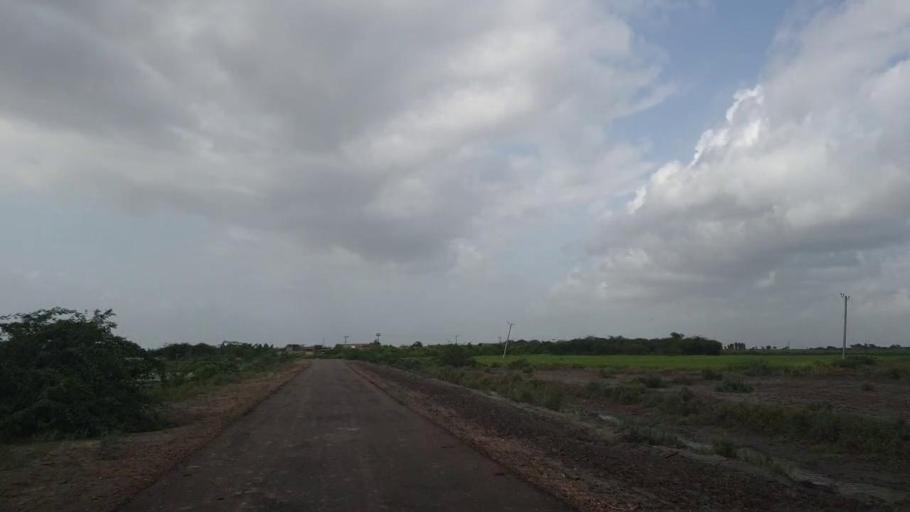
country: PK
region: Sindh
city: Kadhan
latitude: 24.5938
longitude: 69.0561
